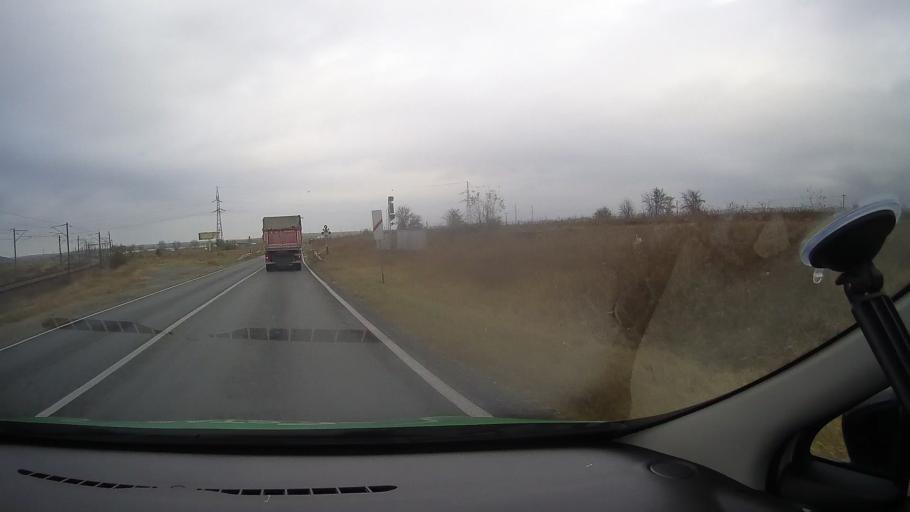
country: RO
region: Constanta
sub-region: Comuna Poarta Alba
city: Poarta Alba
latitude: 44.2325
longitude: 28.3770
